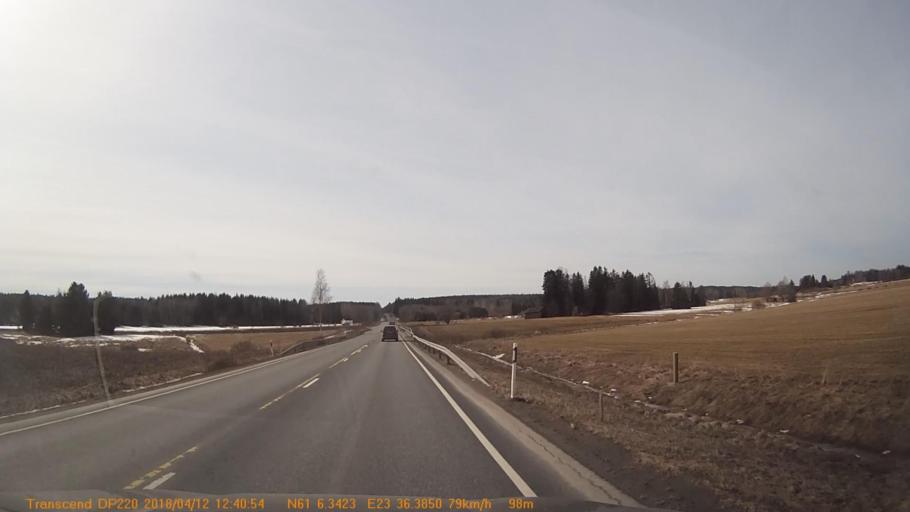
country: FI
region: Pirkanmaa
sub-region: Etelae-Pirkanmaa
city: Urjala
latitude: 61.1057
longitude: 23.6062
